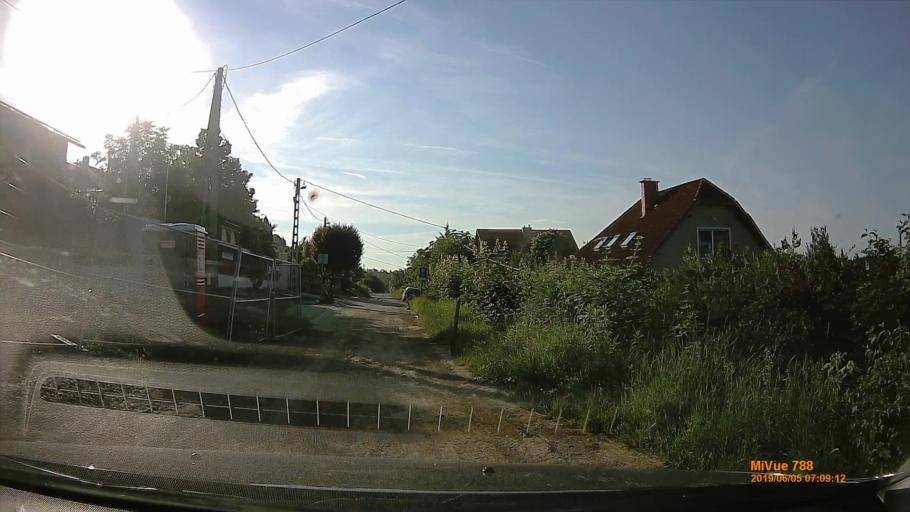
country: HU
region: Pest
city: Urom
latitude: 47.5842
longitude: 19.0270
